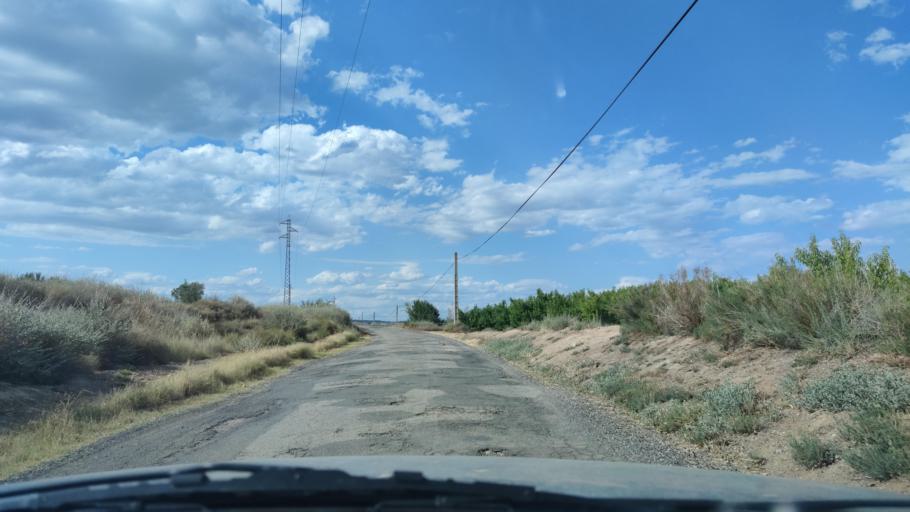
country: ES
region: Catalonia
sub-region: Provincia de Lleida
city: Alcarras
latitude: 41.5872
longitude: 0.5324
